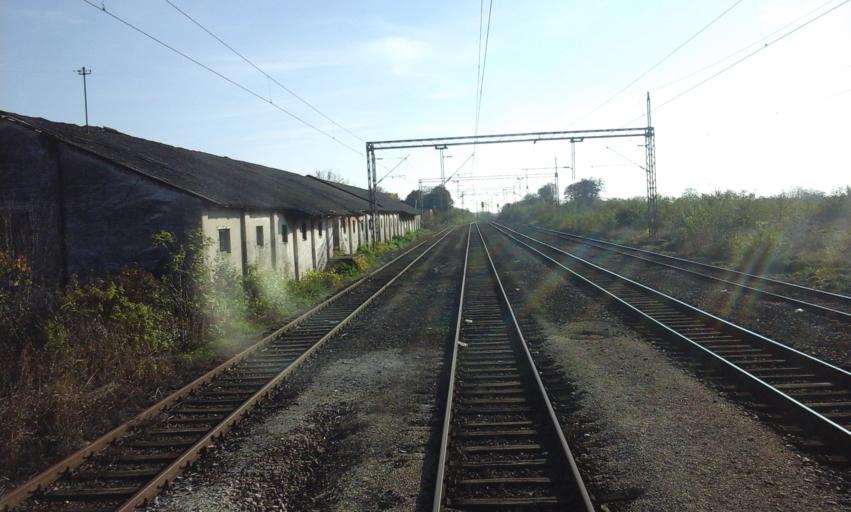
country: RS
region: Autonomna Pokrajina Vojvodina
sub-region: Severnobacki Okrug
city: Mali Igos
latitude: 45.6732
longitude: 19.6491
